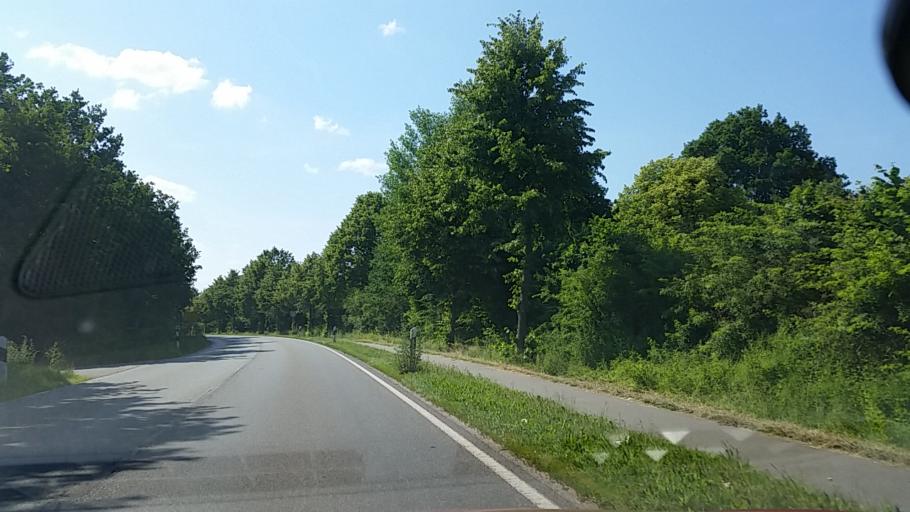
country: DE
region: Schleswig-Holstein
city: Reinbek
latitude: 53.5296
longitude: 10.2483
